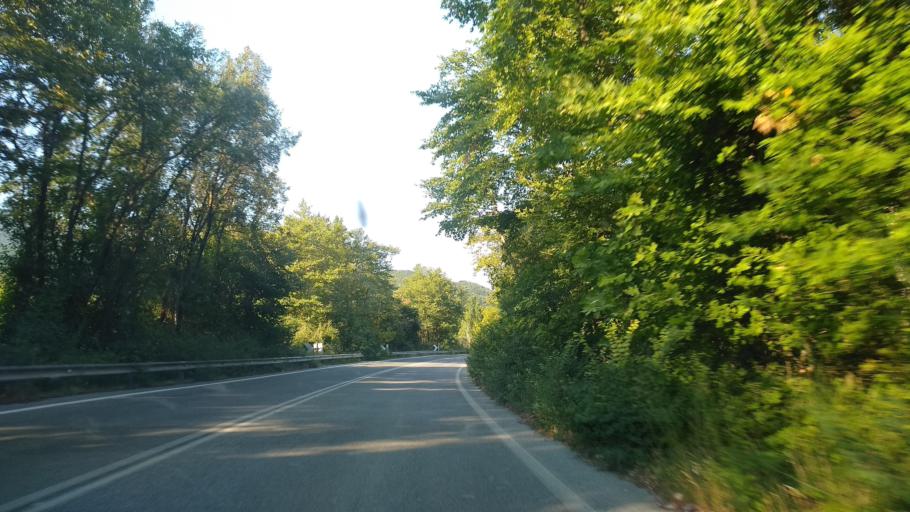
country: GR
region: Central Macedonia
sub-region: Nomos Thessalonikis
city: Stavros
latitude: 40.6755
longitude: 23.6714
